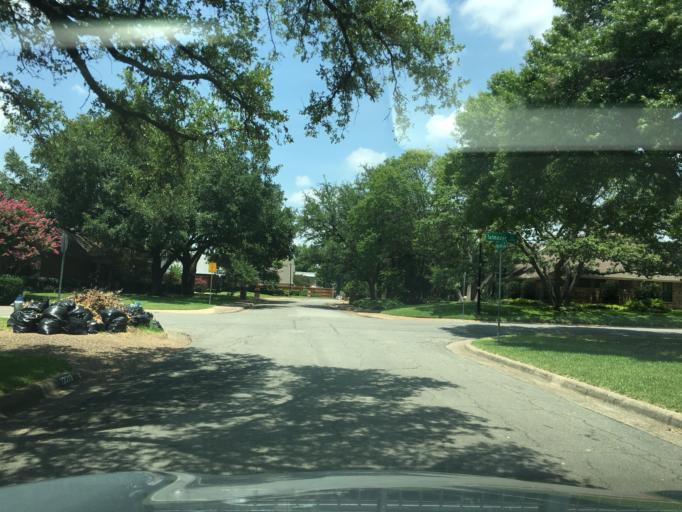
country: US
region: Texas
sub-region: Dallas County
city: Addison
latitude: 32.9148
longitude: -96.7942
